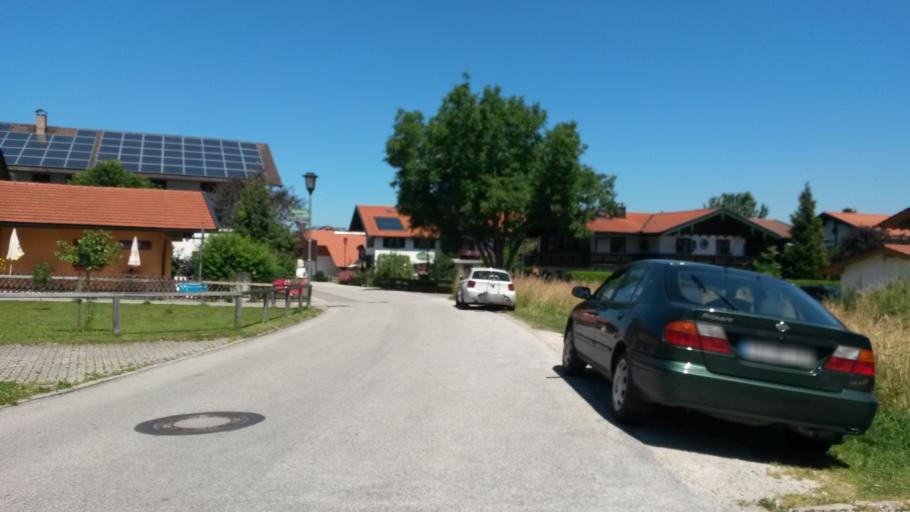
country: DE
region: Bavaria
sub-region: Upper Bavaria
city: Grassau
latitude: 47.7937
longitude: 12.4143
